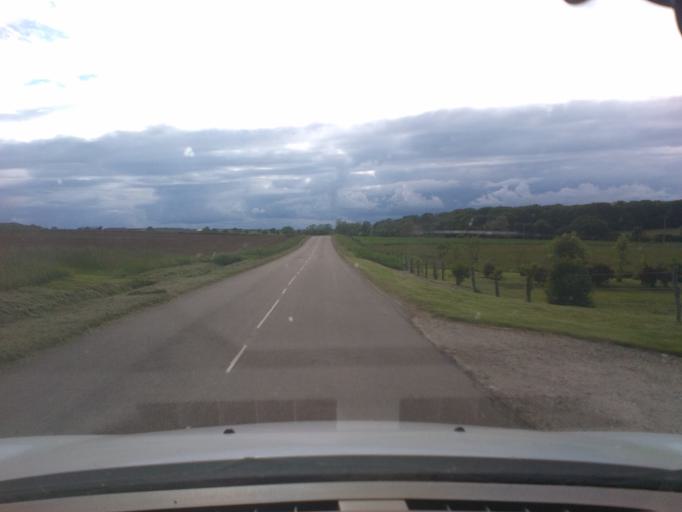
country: FR
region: Lorraine
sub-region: Departement des Vosges
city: Mirecourt
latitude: 48.3303
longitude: 6.0514
